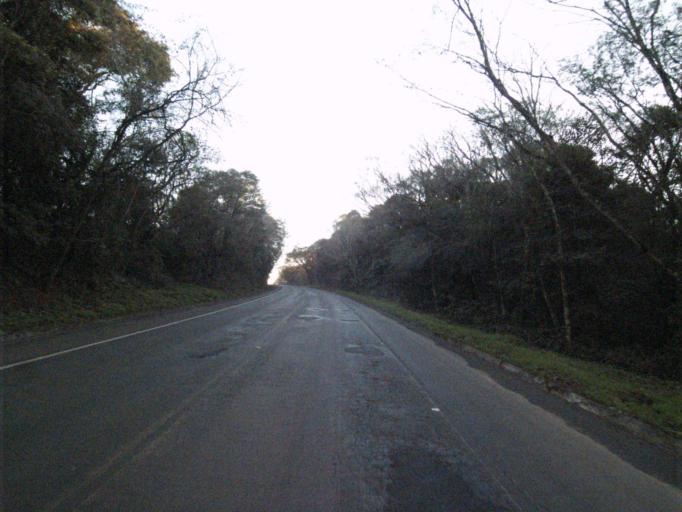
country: BR
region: Santa Catarina
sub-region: Sao Lourenco Do Oeste
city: Sao Lourenco dOeste
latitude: -26.8285
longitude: -53.1153
